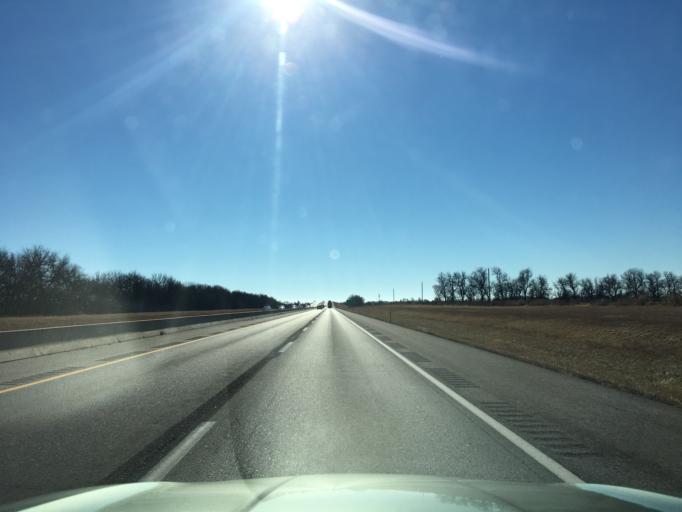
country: US
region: Kansas
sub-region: Sumner County
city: Wellington
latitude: 37.0814
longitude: -97.3386
